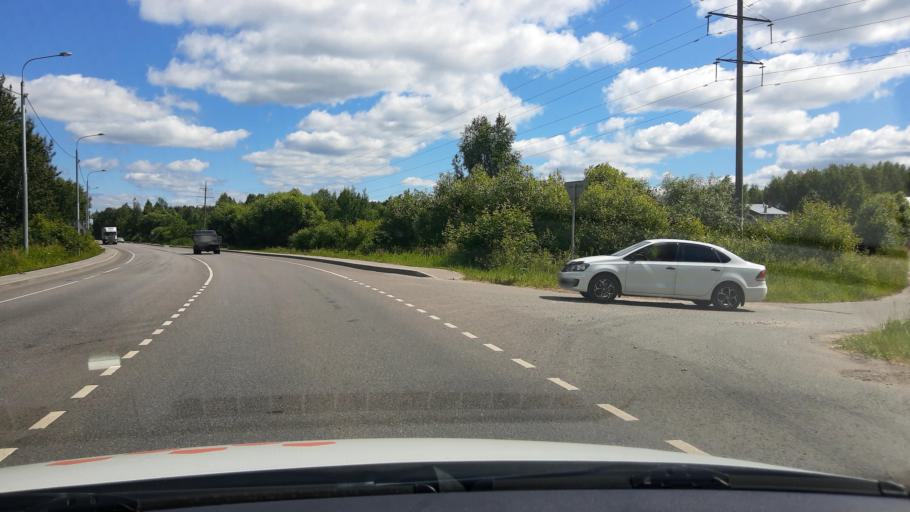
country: RU
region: Moskovskaya
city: Noginsk
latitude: 55.8556
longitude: 38.4043
